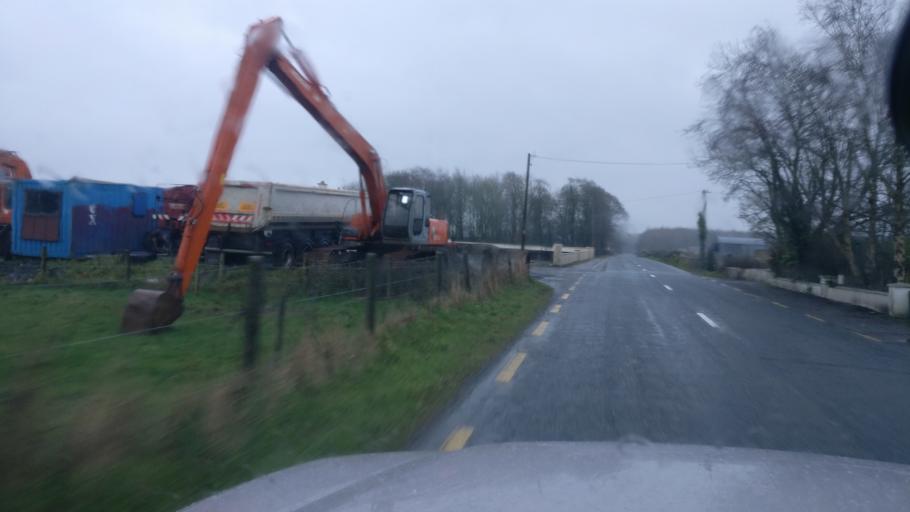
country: IE
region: Connaught
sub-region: County Galway
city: Ballinasloe
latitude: 53.2640
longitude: -8.1905
